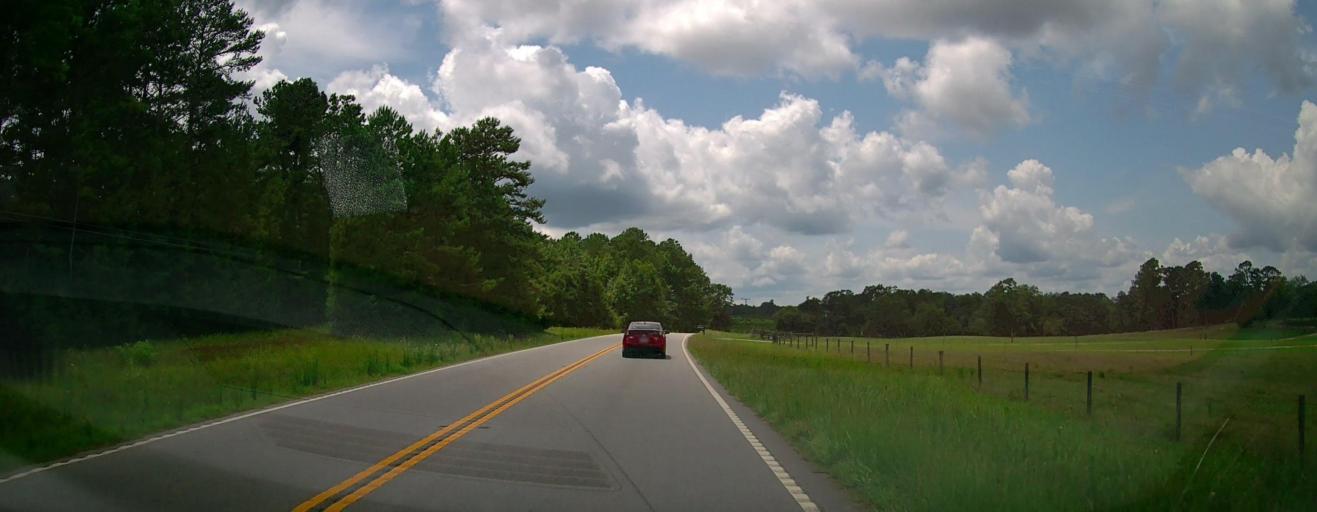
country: US
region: Georgia
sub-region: Meriwether County
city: Greenville
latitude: 32.9832
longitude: -84.6091
